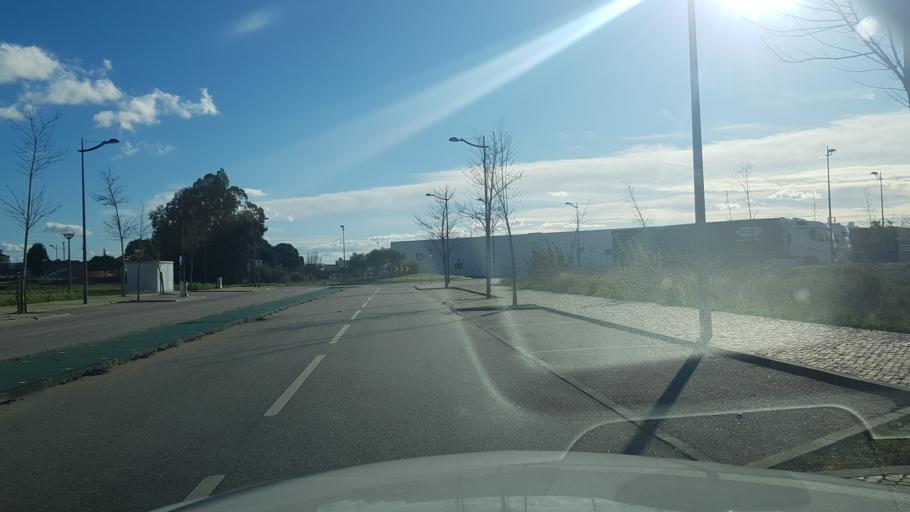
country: PT
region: Santarem
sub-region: Entroncamento
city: Entroncamento
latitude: 39.4742
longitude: -8.4836
